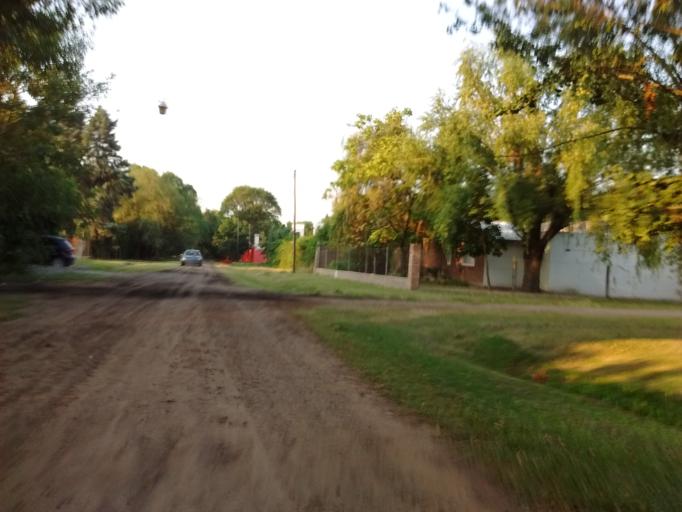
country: AR
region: Santa Fe
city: Funes
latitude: -32.9233
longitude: -60.8307
